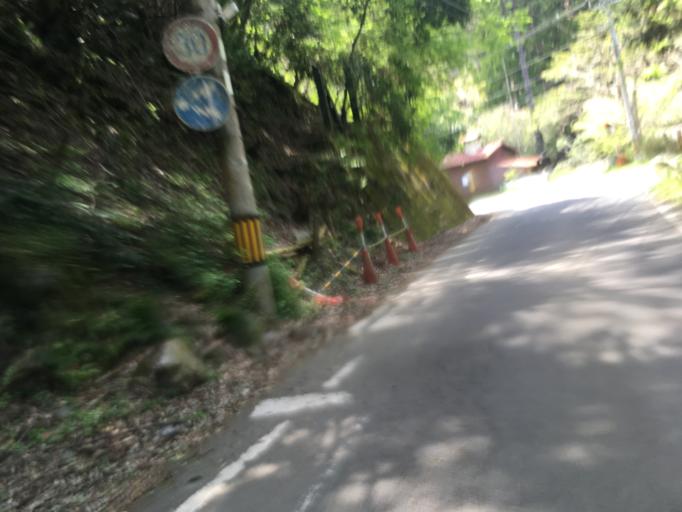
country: JP
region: Kyoto
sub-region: Kyoto-shi
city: Kamigyo-ku
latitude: 35.1090
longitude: 135.7242
